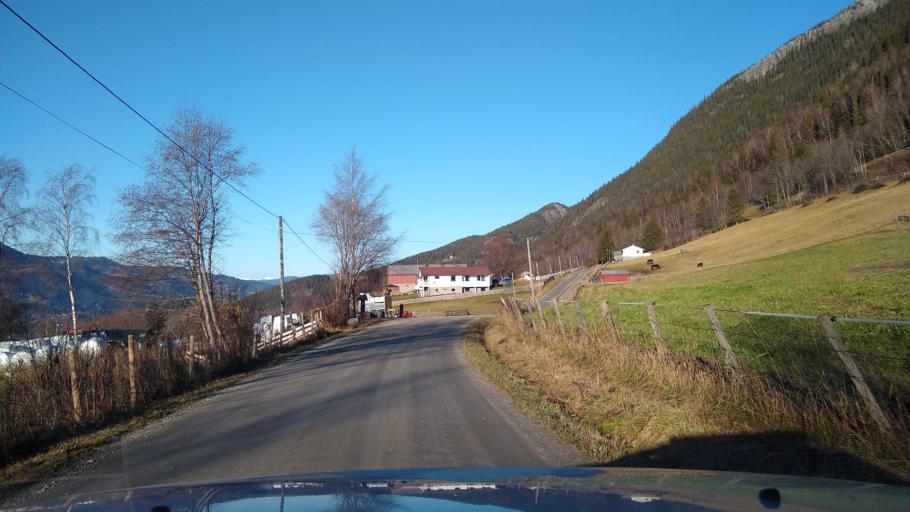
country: NO
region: Oppland
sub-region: Oyer
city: Tretten
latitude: 61.4137
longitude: 10.2400
